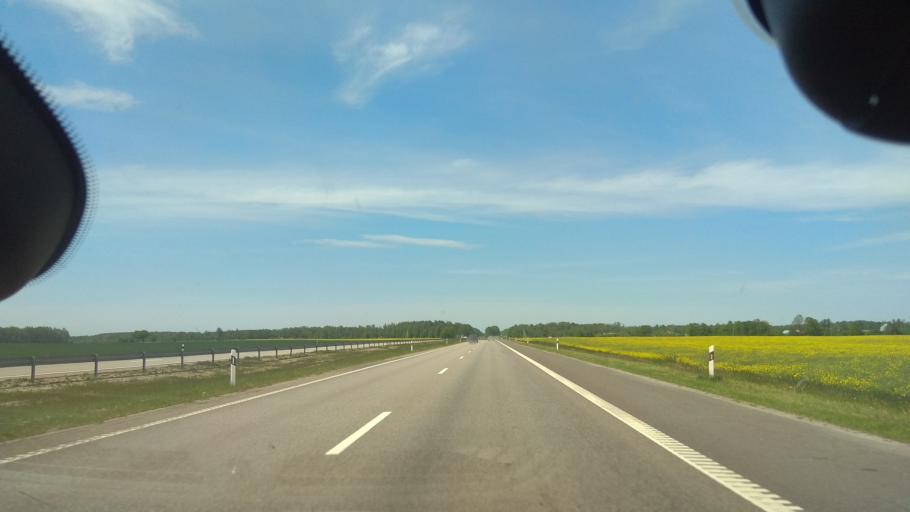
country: LT
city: Vilkija
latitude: 55.1465
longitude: 23.7112
